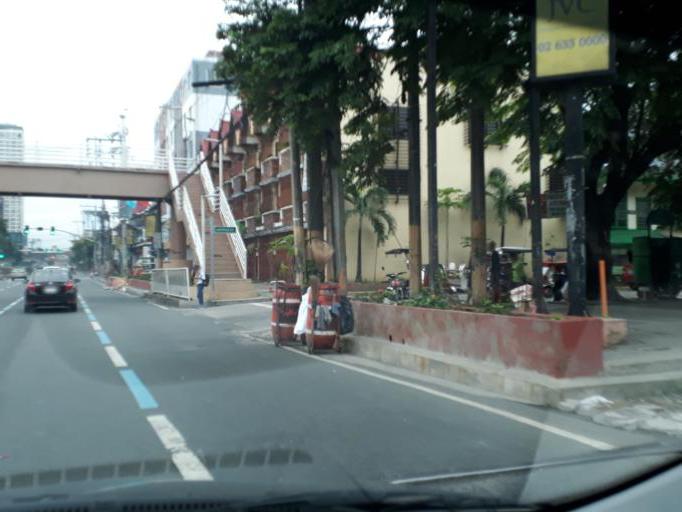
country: PH
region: Metro Manila
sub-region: City of Manila
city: Manila
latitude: 14.6125
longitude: 120.9963
